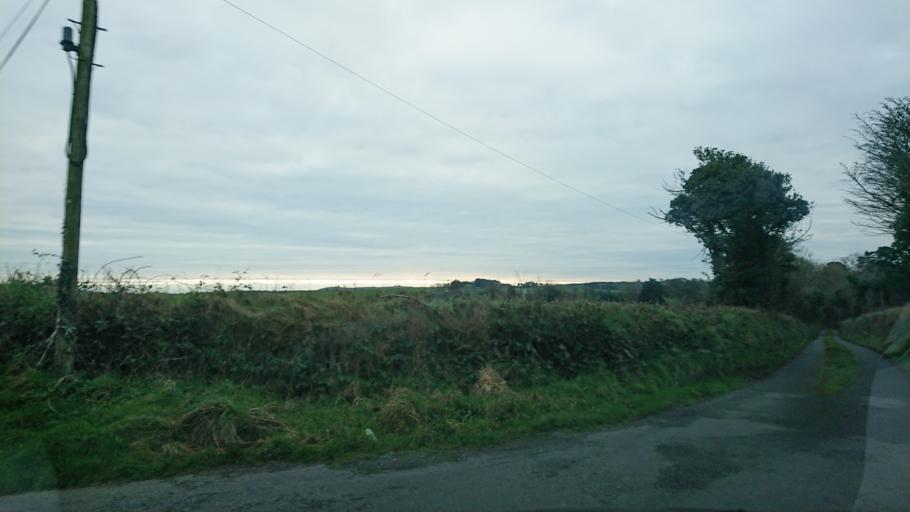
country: IE
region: Leinster
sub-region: Kilkenny
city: Mooncoin
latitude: 52.2187
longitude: -7.2713
